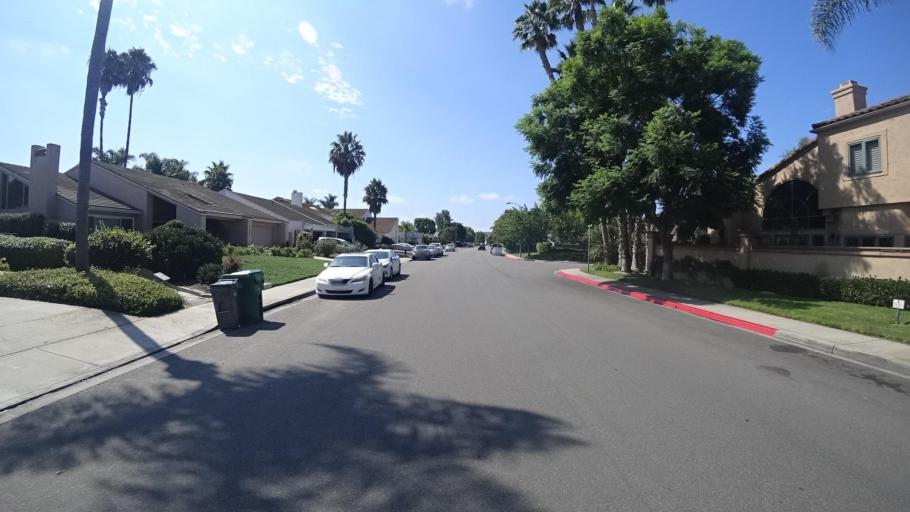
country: US
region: California
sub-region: San Diego County
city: Fairbanks Ranch
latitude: 32.9896
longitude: -117.2130
